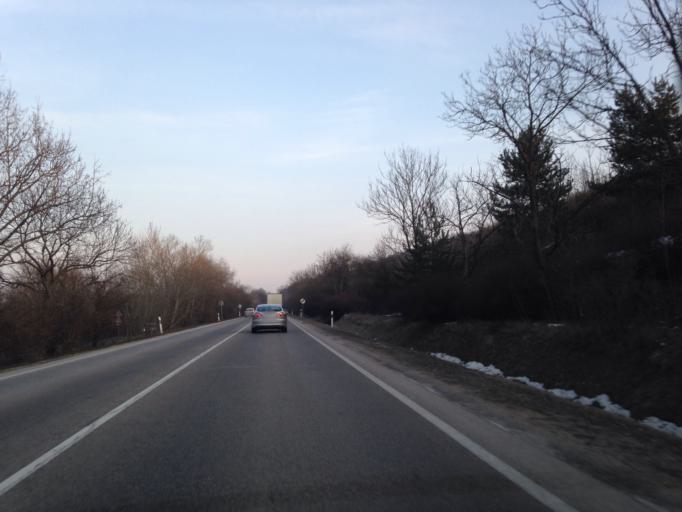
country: HU
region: Fejer
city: Szarliget
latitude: 47.5280
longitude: 18.4643
